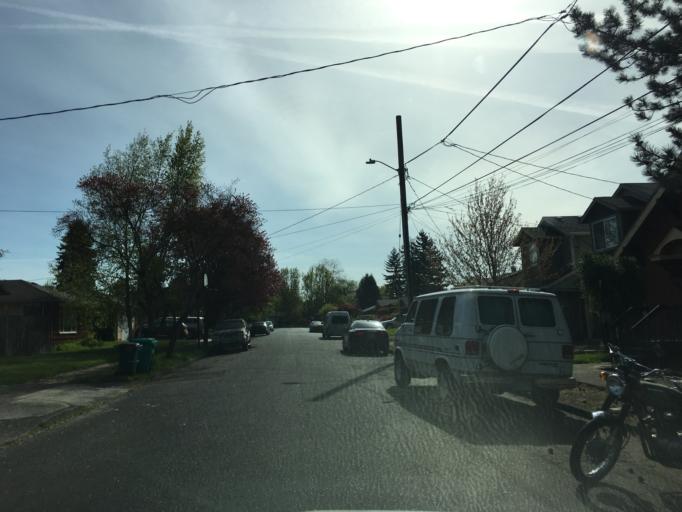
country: US
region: Oregon
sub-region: Multnomah County
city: Lents
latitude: 45.5211
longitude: -122.5699
